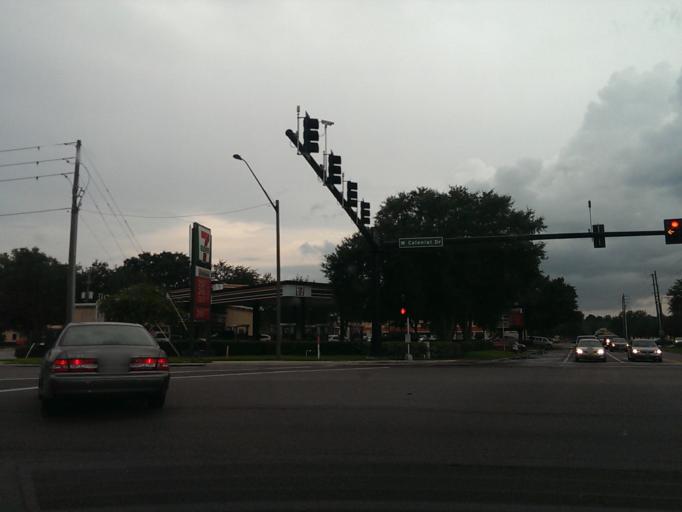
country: US
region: Florida
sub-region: Orange County
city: Winter Garden
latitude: 28.5512
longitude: -81.5873
